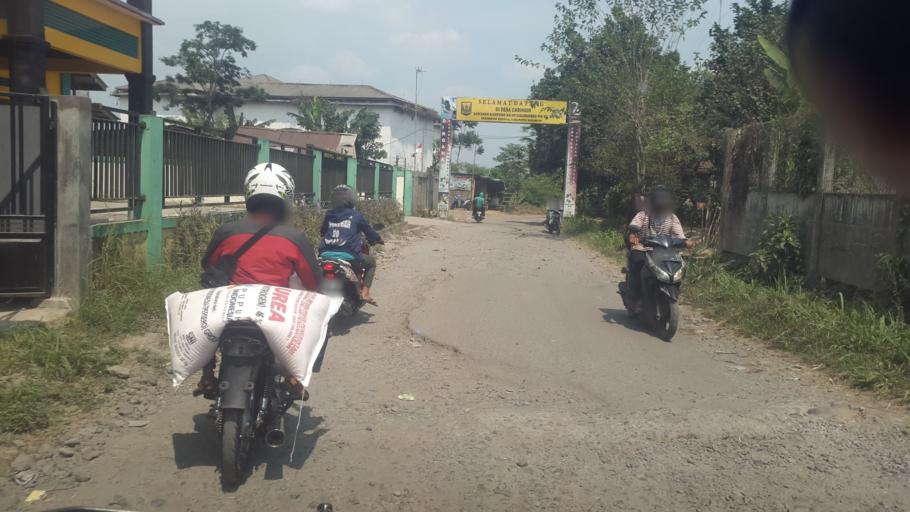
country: ID
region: West Java
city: Cicurug
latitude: -6.7829
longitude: 106.7739
